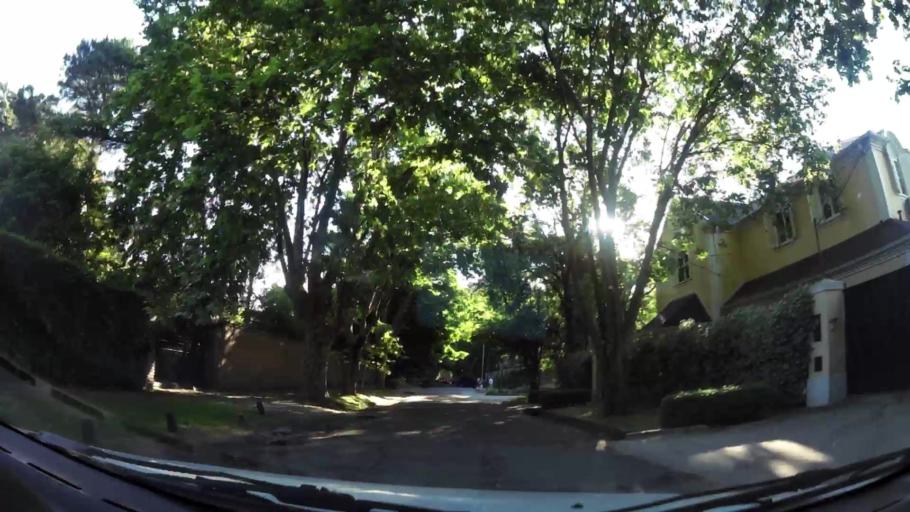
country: AR
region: Buenos Aires
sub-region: Partido de San Isidro
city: San Isidro
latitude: -34.4764
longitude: -58.5483
